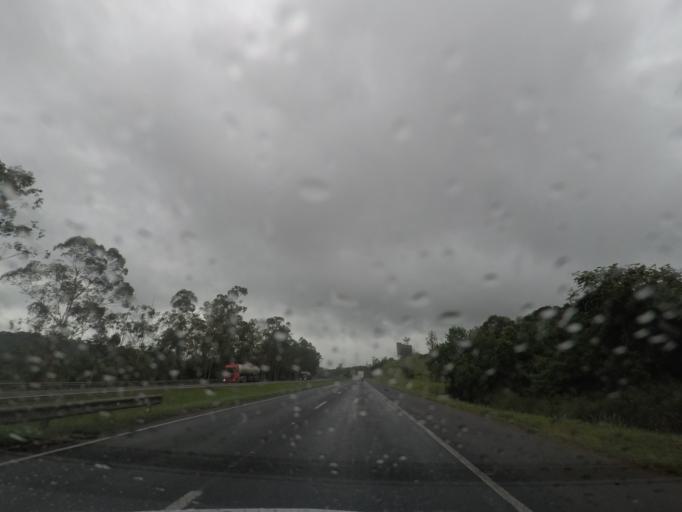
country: BR
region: Sao Paulo
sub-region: Registro
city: Registro
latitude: -24.4197
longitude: -47.7686
